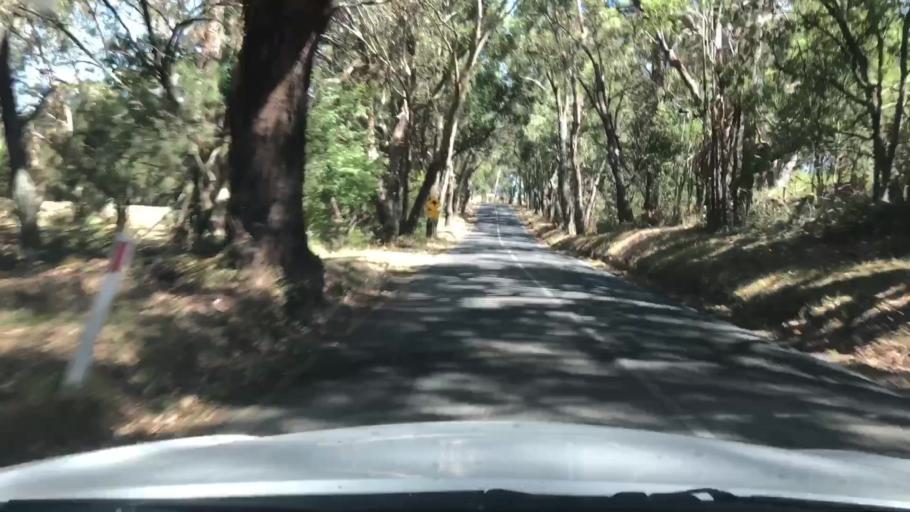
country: AU
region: Victoria
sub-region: Yarra Ranges
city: Macclesfield
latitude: -37.8622
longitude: 145.4786
